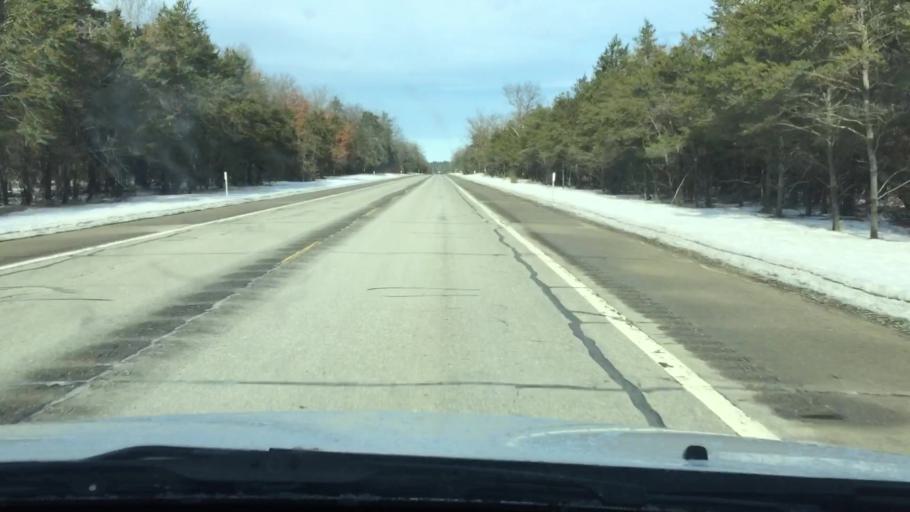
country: US
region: Michigan
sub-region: Wexford County
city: Manton
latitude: 44.5325
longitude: -85.3829
